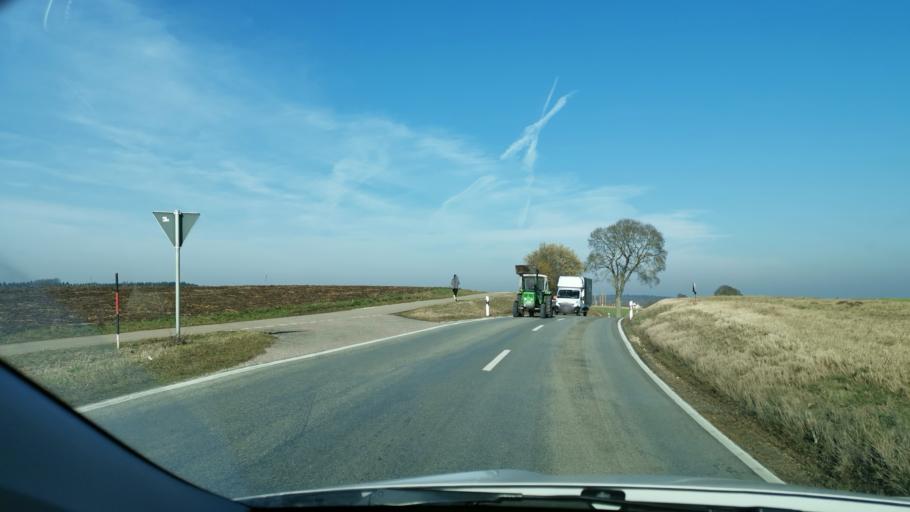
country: DE
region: Bavaria
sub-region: Swabia
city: Holzheim
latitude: 48.5985
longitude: 10.9514
